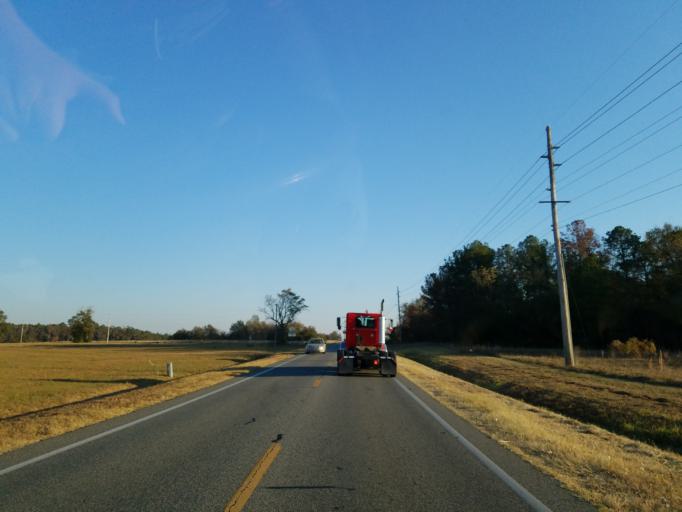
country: US
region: Georgia
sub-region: Crisp County
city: Cordele
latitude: 31.9476
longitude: -83.7435
